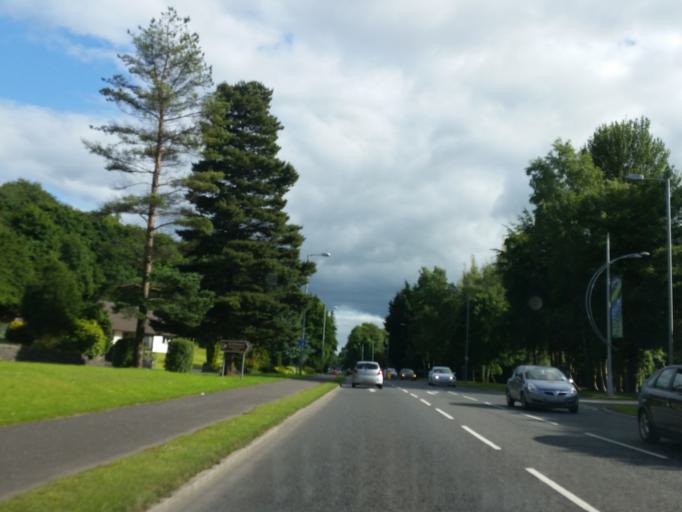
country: GB
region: Northern Ireland
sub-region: Fermanagh District
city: Enniskillen
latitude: 54.3384
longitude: -7.6252
